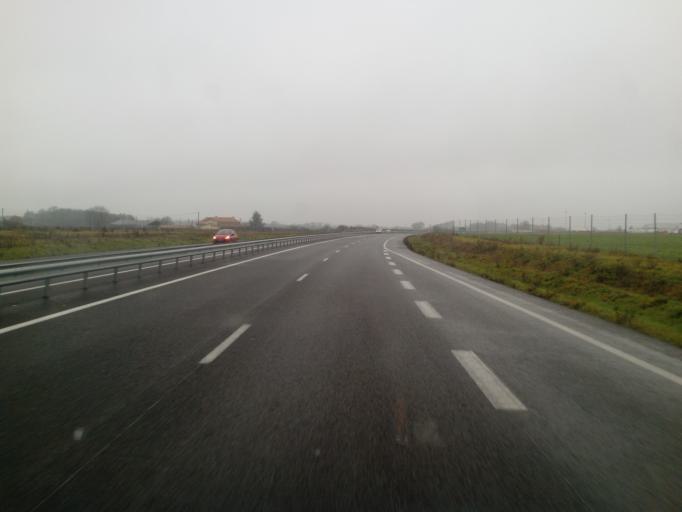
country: FR
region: Poitou-Charentes
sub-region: Departement de la Vienne
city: Savigny-Levescault
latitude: 46.4863
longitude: 0.5118
